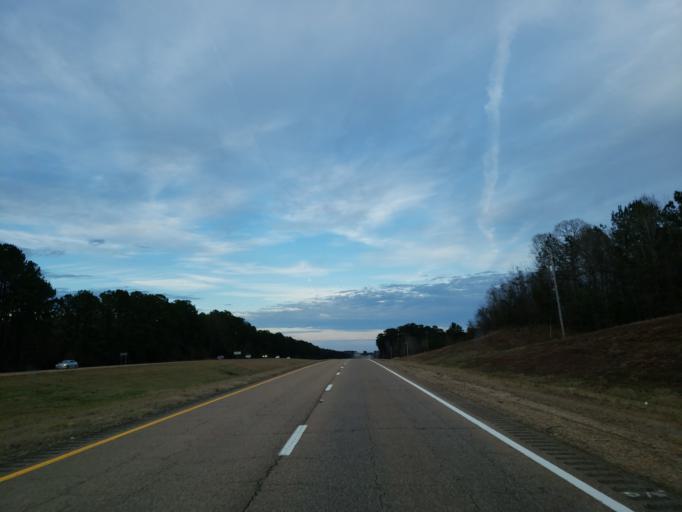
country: US
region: Mississippi
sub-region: Lauderdale County
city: Meridian Station
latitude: 32.4932
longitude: -88.5797
